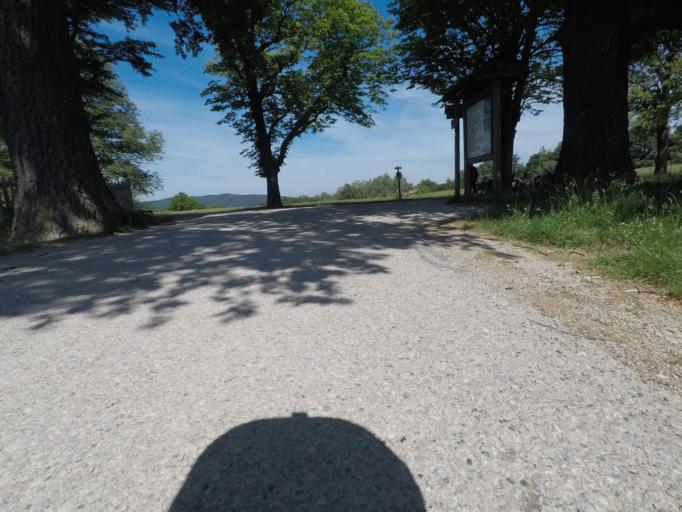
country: AT
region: Lower Austria
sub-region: Politischer Bezirk Modling
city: Laab im Walde
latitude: 48.1787
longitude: 16.2315
